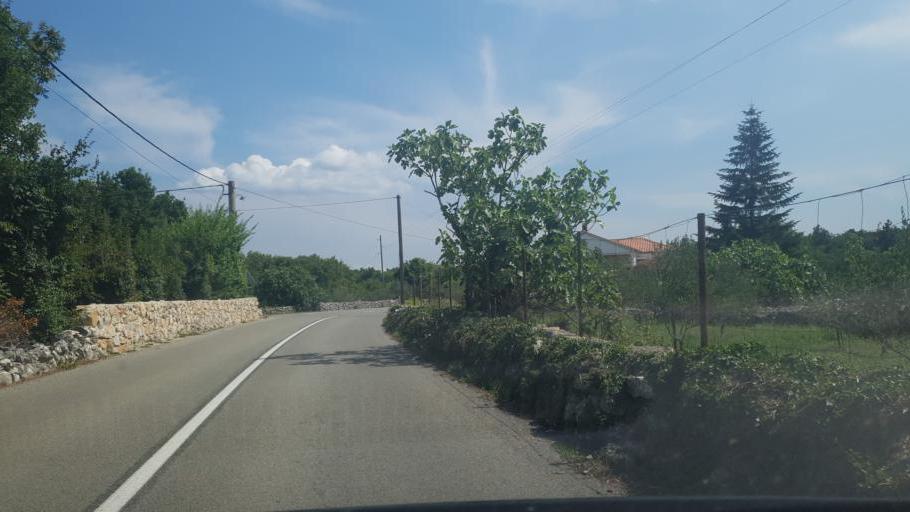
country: HR
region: Primorsko-Goranska
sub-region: Grad Crikvenica
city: Crikvenica
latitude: 45.1194
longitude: 14.6297
